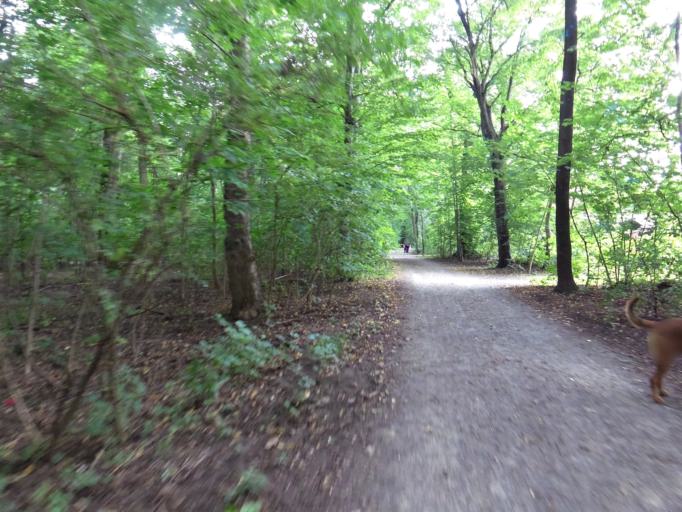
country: DE
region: Saxony
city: Leipzig
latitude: 51.3526
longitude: 12.3266
